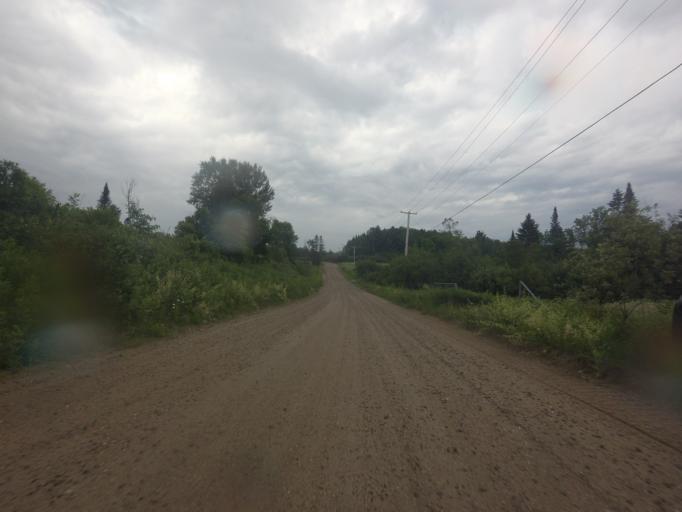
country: CA
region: Quebec
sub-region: Outaouais
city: Maniwaki
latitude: 46.4488
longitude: -75.9401
